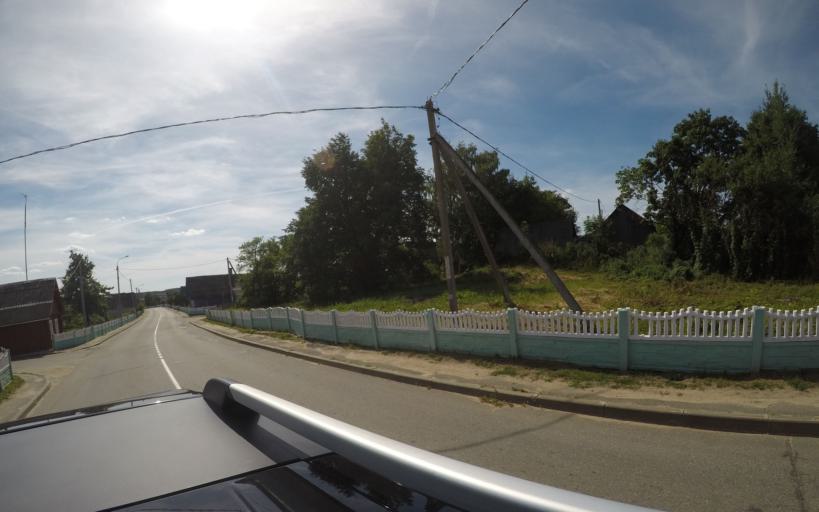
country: BY
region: Grodnenskaya
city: Hal'shany
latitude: 54.2602
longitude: 26.0171
